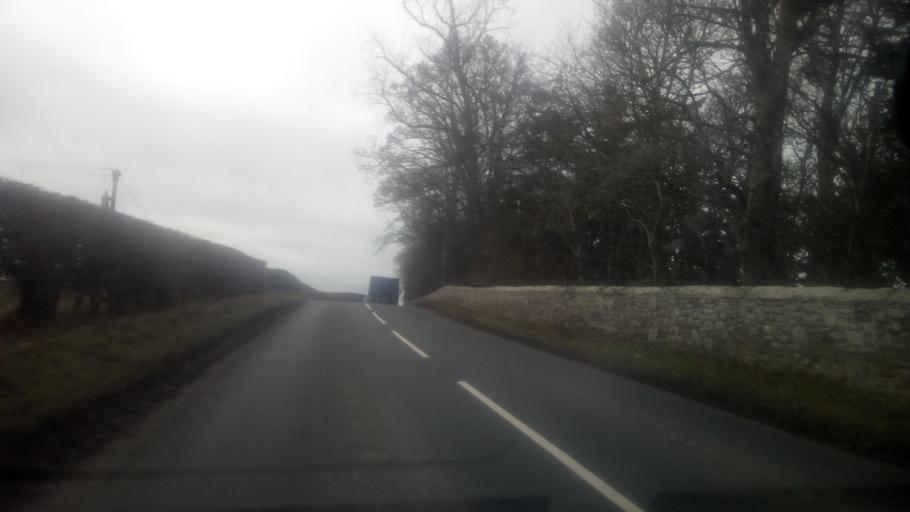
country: GB
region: Scotland
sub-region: The Scottish Borders
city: Kelso
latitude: 55.5927
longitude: -2.4653
